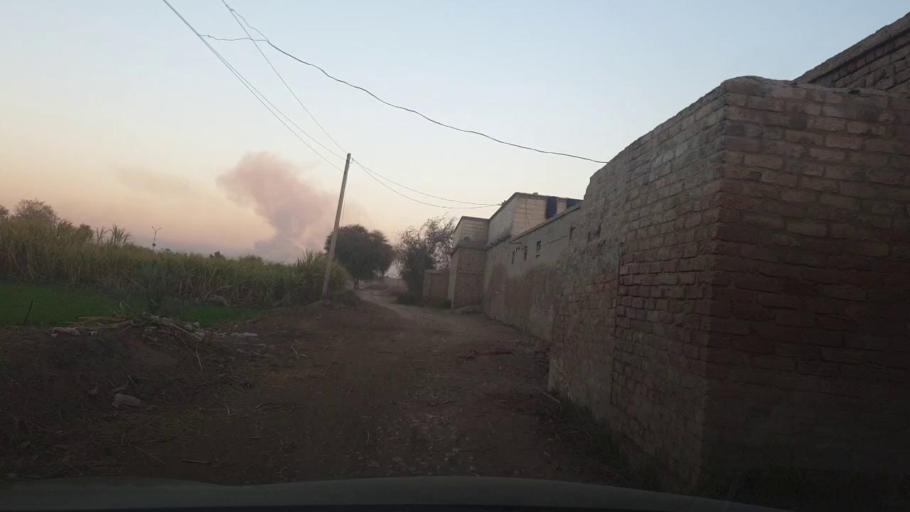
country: PK
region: Sindh
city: Ghotki
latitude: 28.0551
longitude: 69.3597
